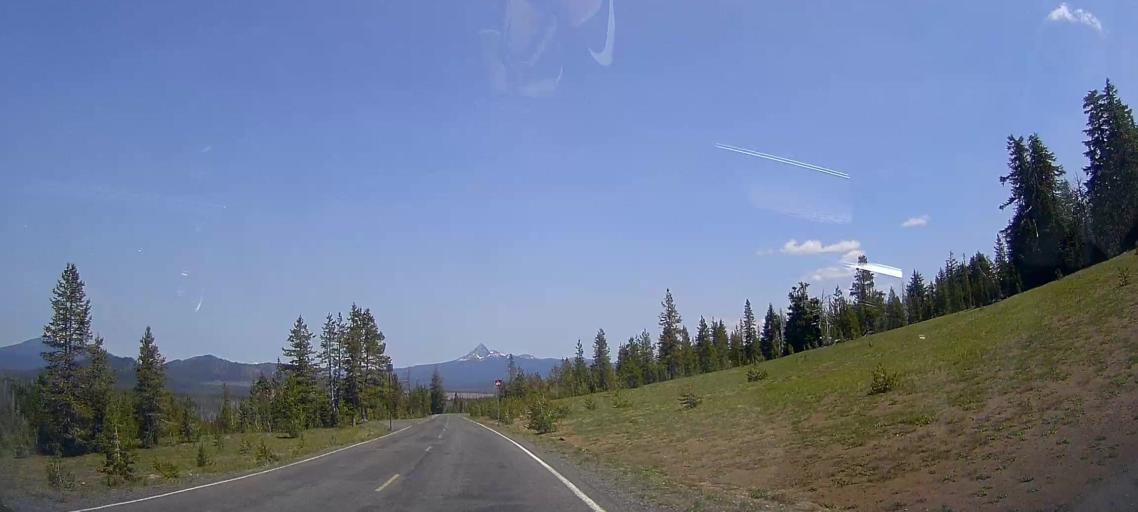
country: US
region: Oregon
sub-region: Jackson County
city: Shady Cove
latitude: 42.9894
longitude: -122.1437
